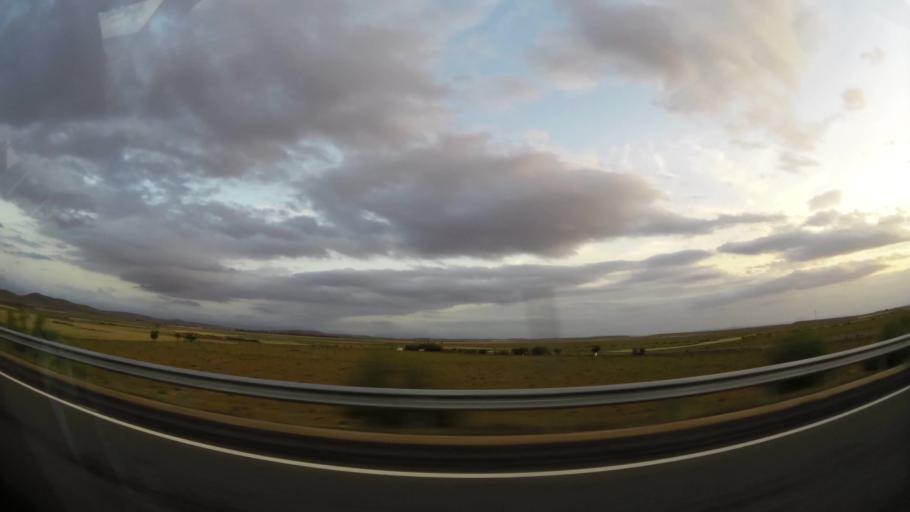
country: MA
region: Oriental
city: El Aioun
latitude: 34.6008
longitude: -2.7375
